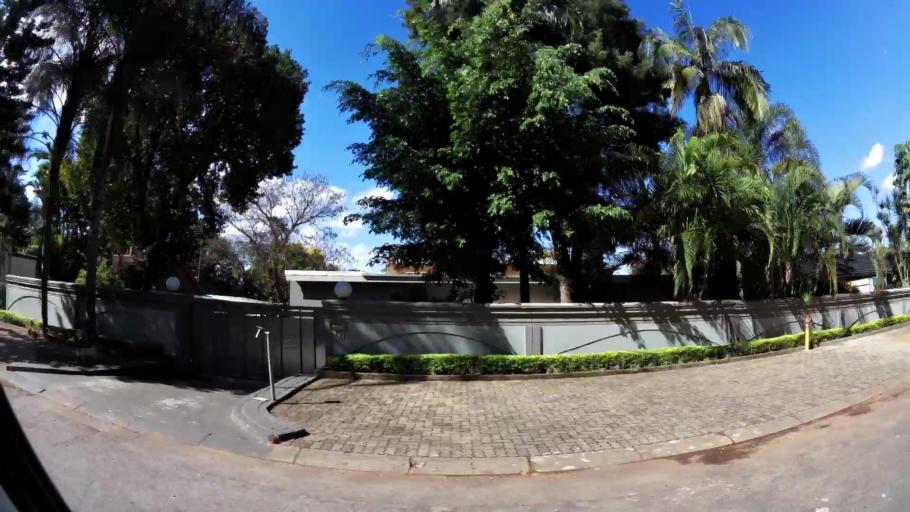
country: ZA
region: Limpopo
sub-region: Mopani District Municipality
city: Tzaneen
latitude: -23.8141
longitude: 30.1568
